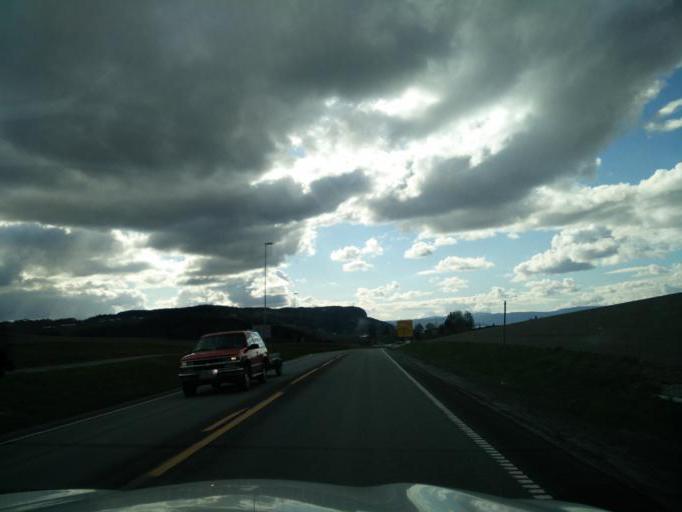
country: NO
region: Sor-Trondelag
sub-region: Melhus
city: Melhus
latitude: 63.3220
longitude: 10.3104
